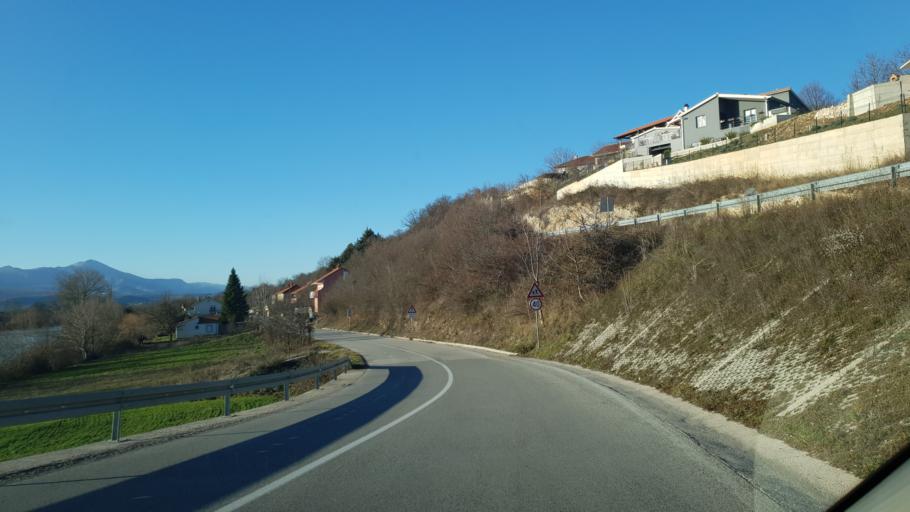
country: HR
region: Splitsko-Dalmatinska
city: Gala
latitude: 43.7305
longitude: 16.6947
